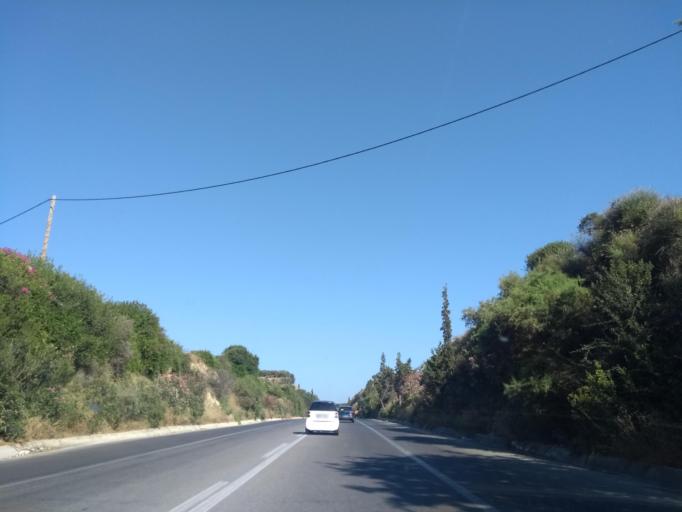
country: GR
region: Crete
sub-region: Nomos Chanias
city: Agia Marina
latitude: 35.5104
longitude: 23.9315
